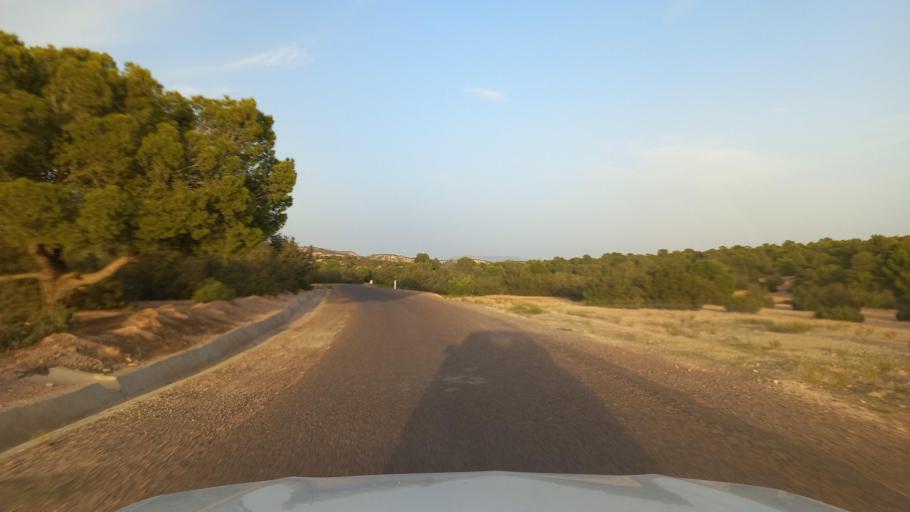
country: TN
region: Al Qasrayn
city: Sbiba
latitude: 35.4099
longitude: 8.9193
